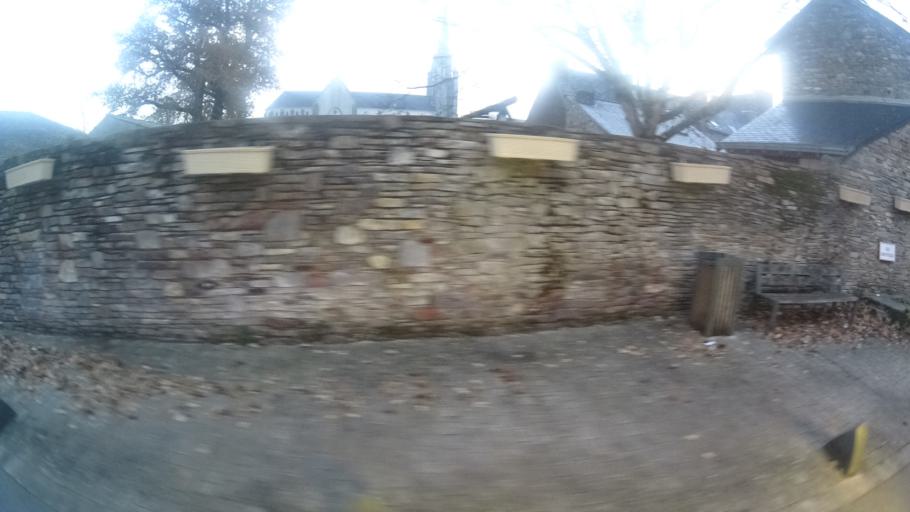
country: FR
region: Pays de la Loire
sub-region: Departement de la Loire-Atlantique
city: Saint-Nicolas-de-Redon
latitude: 47.6442
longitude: -2.0703
